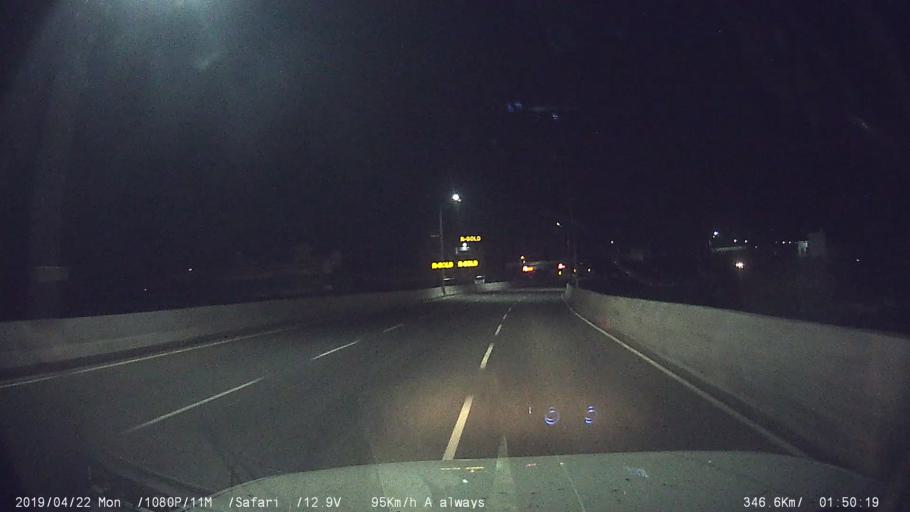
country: IN
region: Tamil Nadu
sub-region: Erode
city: Bhavani
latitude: 11.4318
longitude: 77.6770
